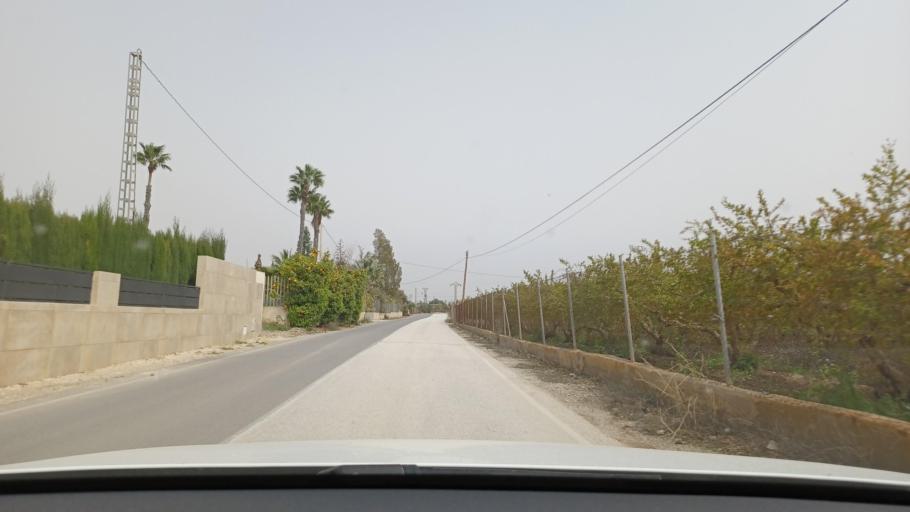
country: ES
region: Valencia
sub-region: Provincia de Alicante
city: Elche
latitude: 38.2387
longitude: -0.6923
